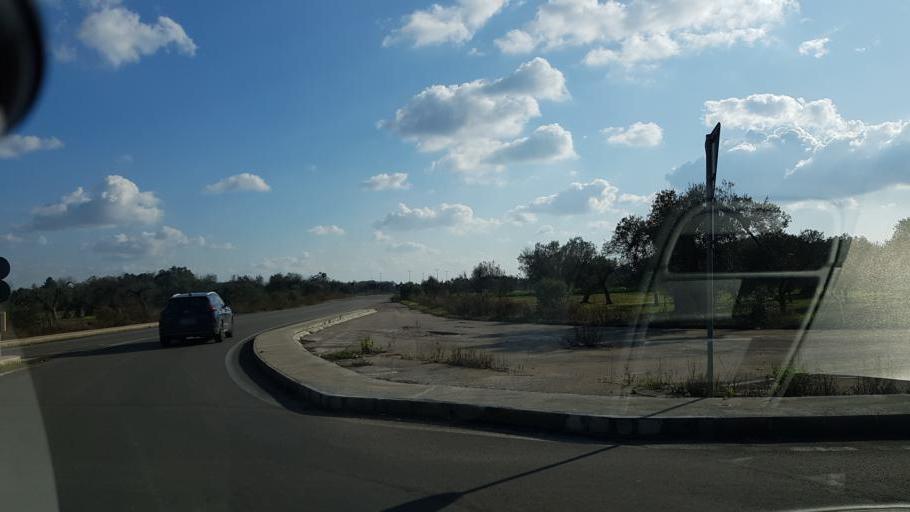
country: IT
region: Apulia
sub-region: Provincia di Lecce
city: Veglie
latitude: 40.3390
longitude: 17.9800
